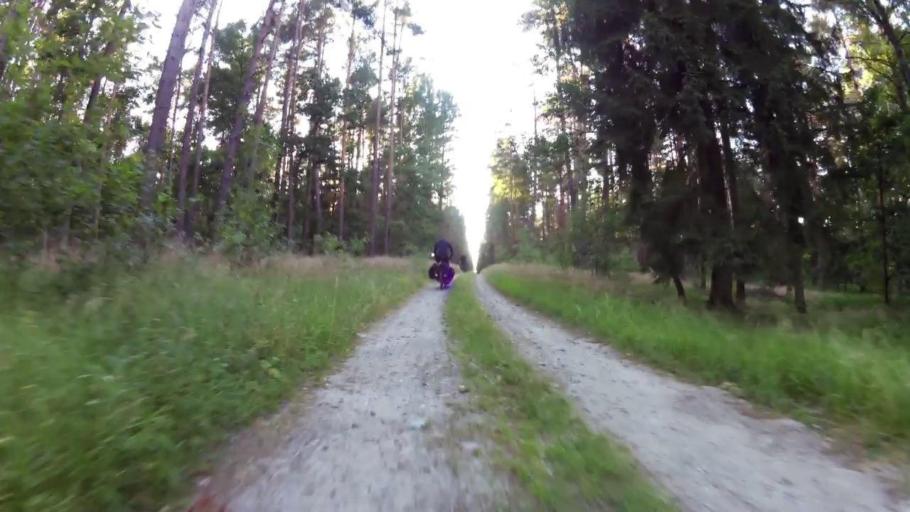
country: PL
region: West Pomeranian Voivodeship
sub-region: Powiat lobeski
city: Lobez
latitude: 53.7395
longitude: 15.6564
